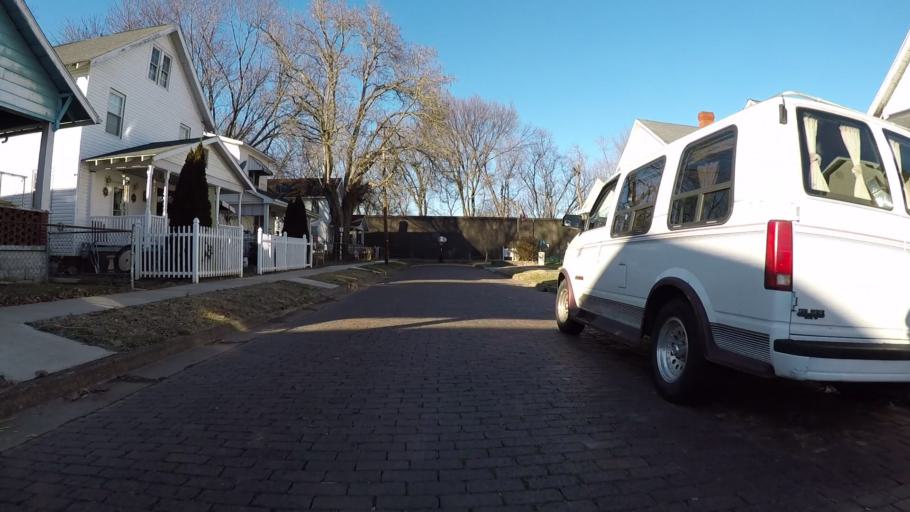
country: US
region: West Virginia
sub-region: Cabell County
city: Pea Ridge
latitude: 38.4301
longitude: -82.3816
